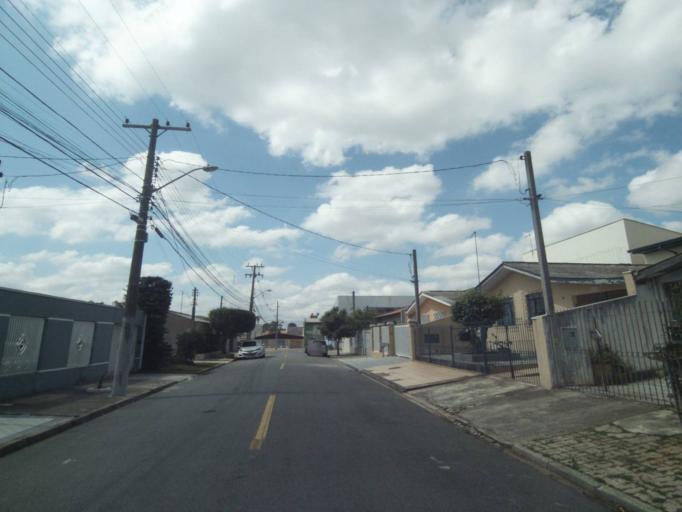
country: BR
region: Parana
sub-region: Curitiba
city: Curitiba
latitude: -25.5127
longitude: -49.3216
